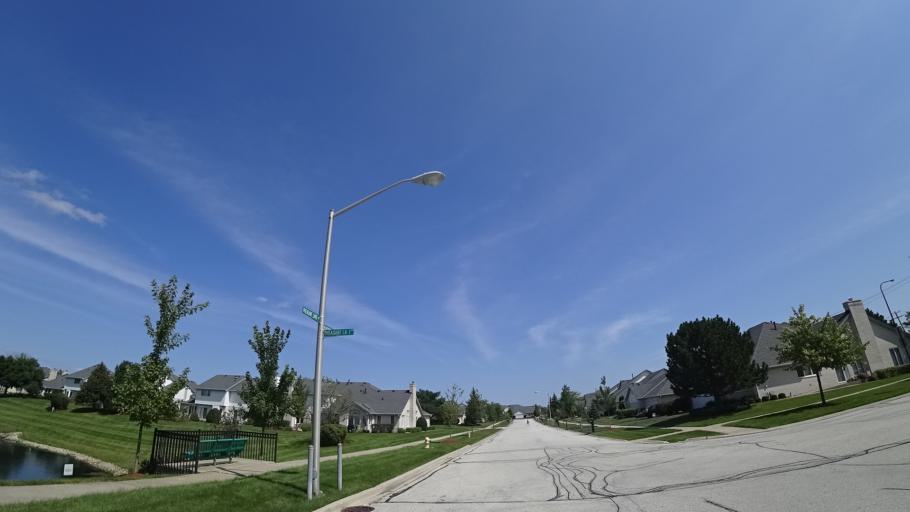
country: US
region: Illinois
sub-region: Cook County
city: Orland Hills
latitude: 41.5586
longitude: -87.8349
